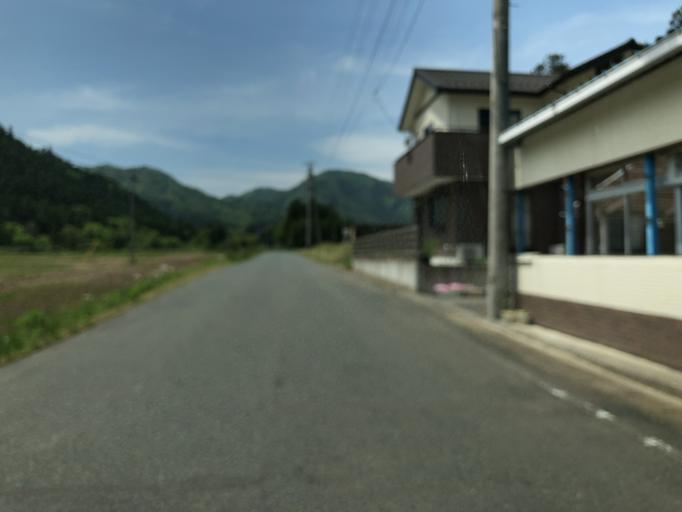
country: JP
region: Fukushima
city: Namie
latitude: 37.6891
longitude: 140.9020
